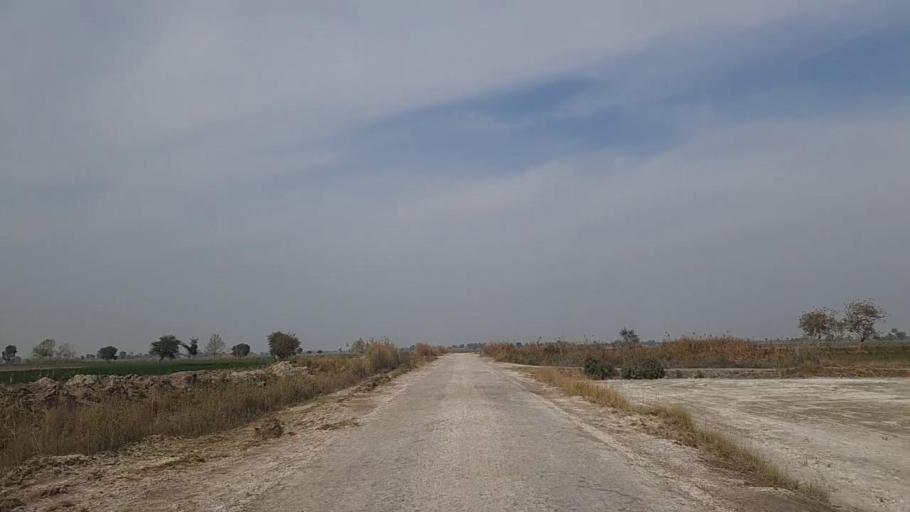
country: PK
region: Sindh
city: Daur
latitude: 26.4686
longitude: 68.4027
